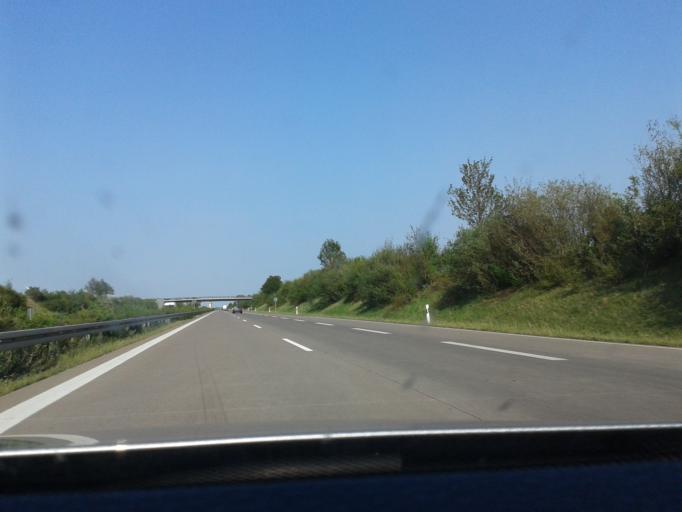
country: DE
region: Saxony-Anhalt
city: Allstedt
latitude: 51.4348
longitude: 11.4297
